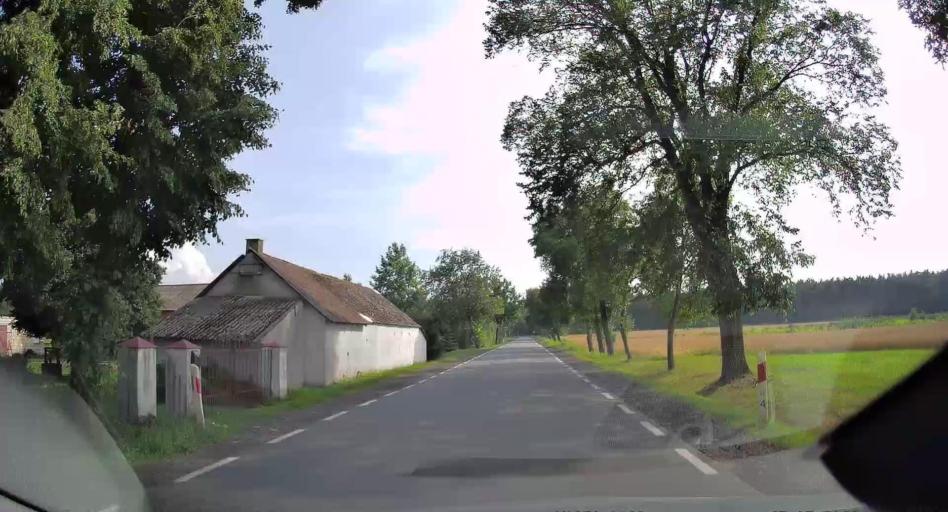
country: PL
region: Lodz Voivodeship
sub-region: Powiat tomaszowski
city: Rzeczyca
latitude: 51.5805
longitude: 20.2842
